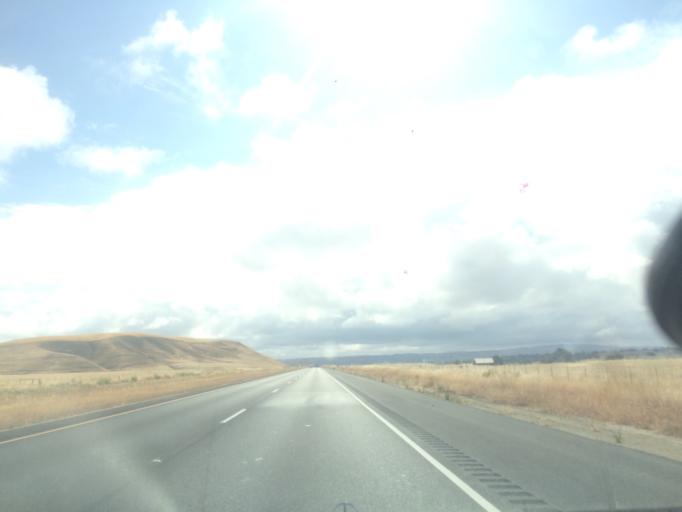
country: US
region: California
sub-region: San Luis Obispo County
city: Shandon
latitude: 35.6601
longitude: -120.4590
